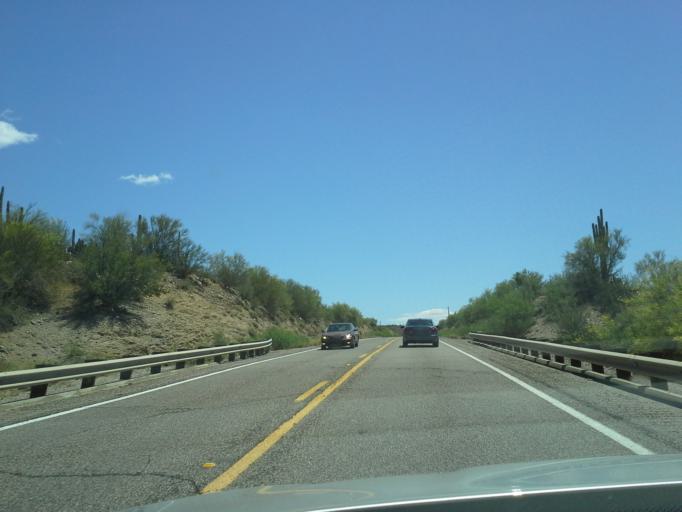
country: US
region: Arizona
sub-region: Pinal County
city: Kearny
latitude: 33.1077
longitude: -110.9488
